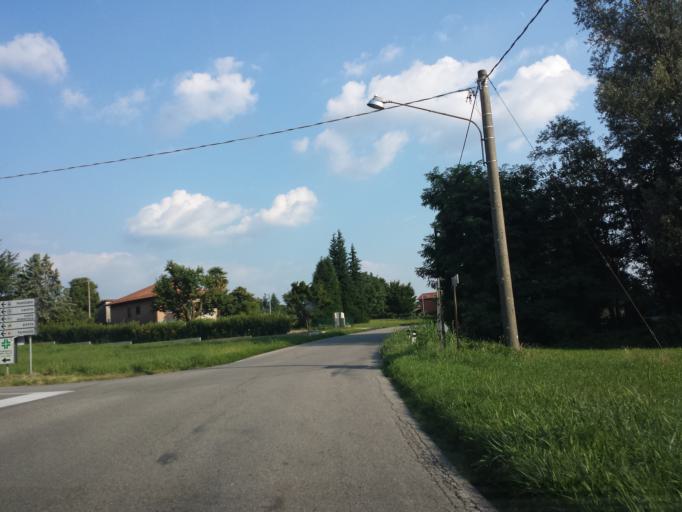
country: IT
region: Lombardy
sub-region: Provincia di Varese
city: Monvalle
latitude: 45.8552
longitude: 8.6249
